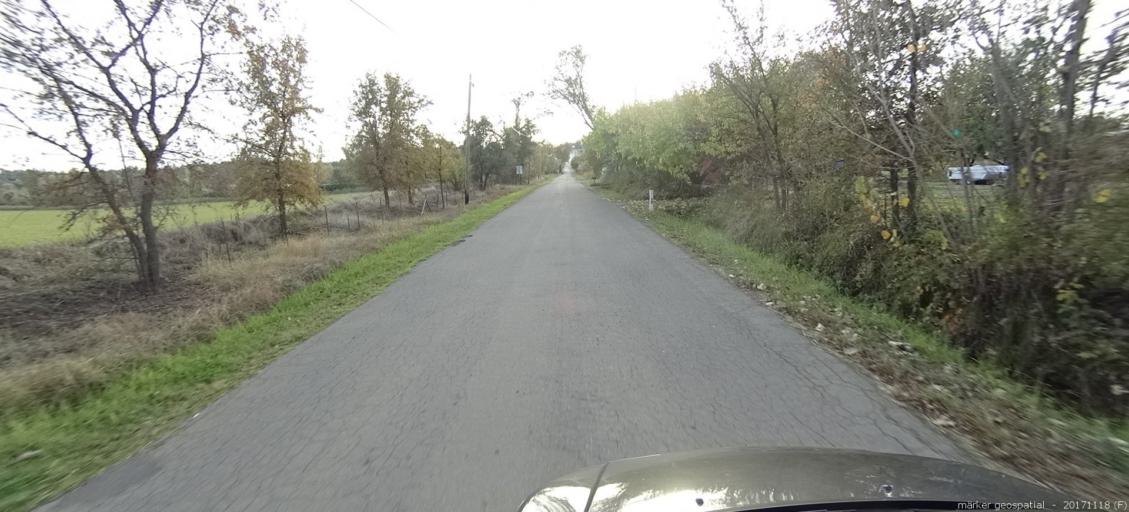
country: US
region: California
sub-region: Shasta County
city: Anderson
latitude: 40.4564
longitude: -122.3188
